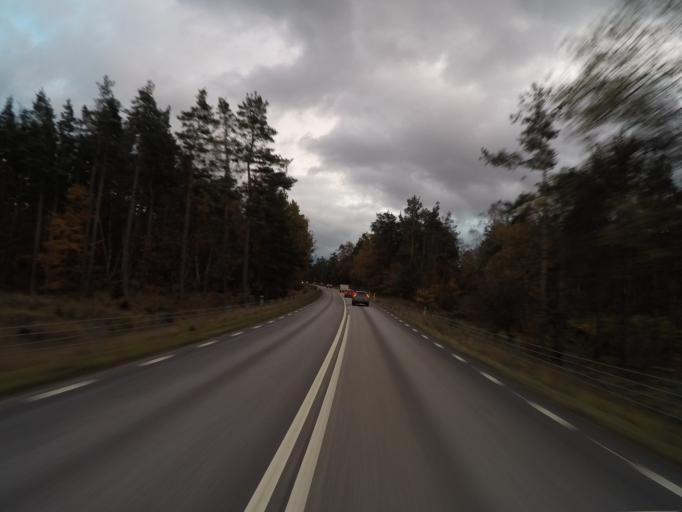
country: SE
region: Skane
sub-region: Kristianstads Kommun
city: Degeberga
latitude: 55.8592
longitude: 14.0914
